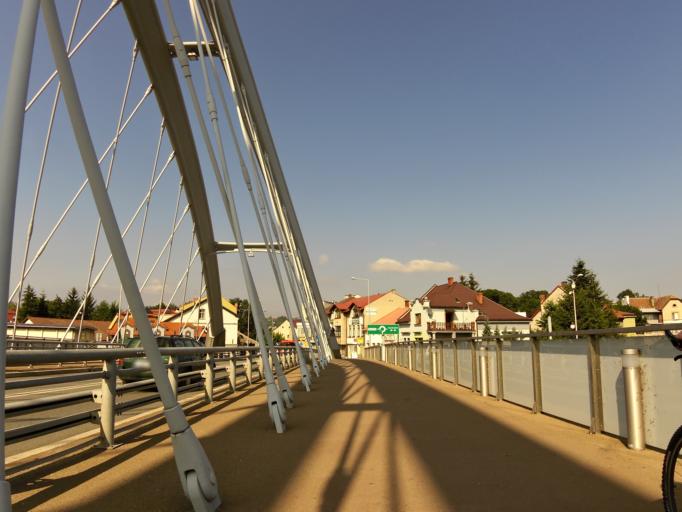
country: PL
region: Silesian Voivodeship
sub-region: Powiat zywiecki
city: Zywiec
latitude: 49.6859
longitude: 19.1935
